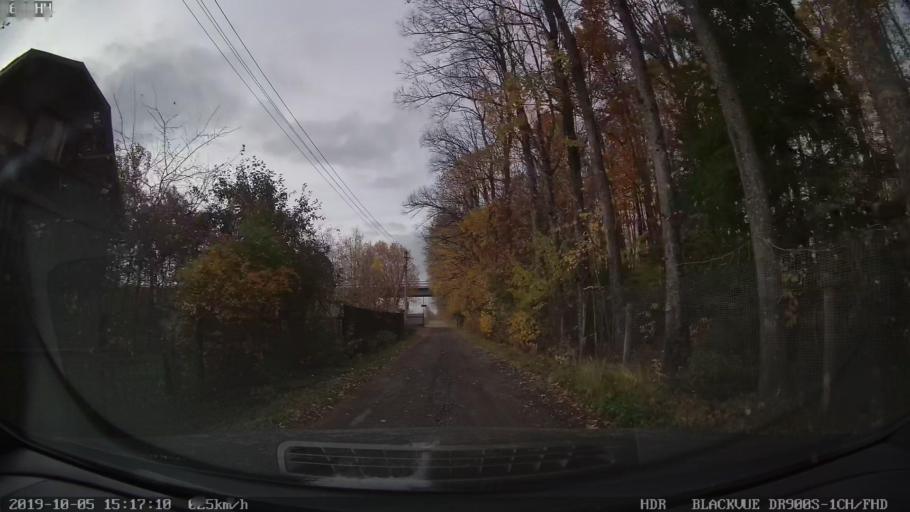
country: RU
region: Moskovskaya
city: Solnechnogorsk
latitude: 56.2162
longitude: 36.9057
